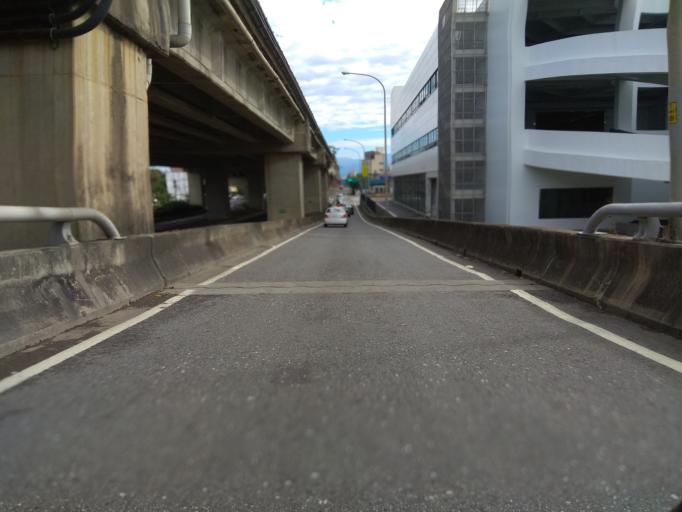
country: TW
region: Taiwan
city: Daxi
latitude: 24.9326
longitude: 121.1965
